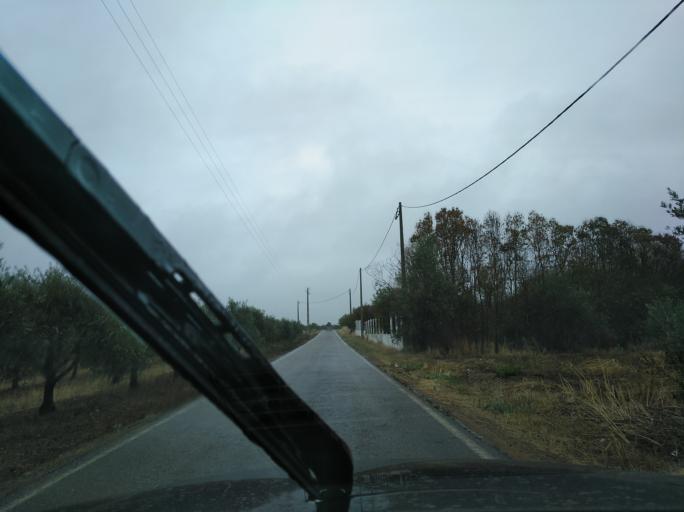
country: PT
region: Portalegre
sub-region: Campo Maior
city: Campo Maior
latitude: 38.9502
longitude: -7.0859
